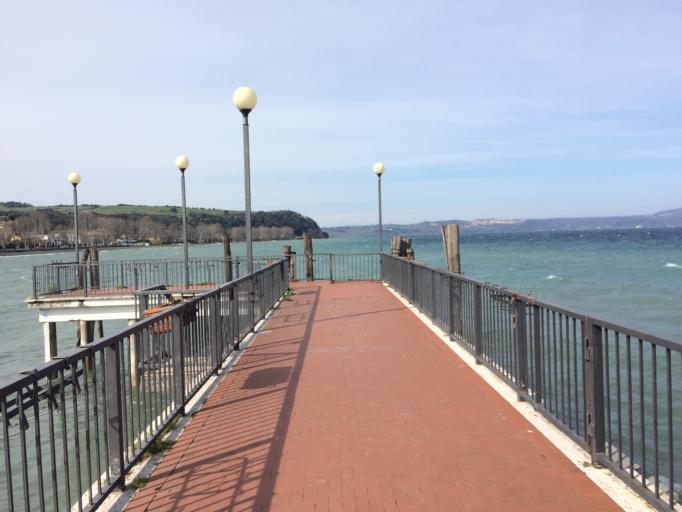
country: IT
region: Latium
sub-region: Citta metropolitana di Roma Capitale
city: Anguillara Sabazia
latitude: 42.0930
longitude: 12.2679
